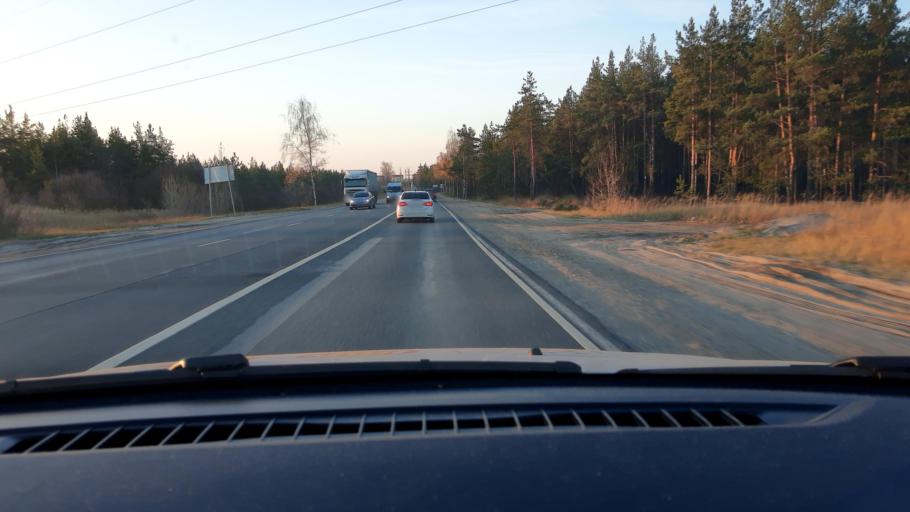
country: RU
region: Nizjnij Novgorod
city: Dzerzhinsk
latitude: 56.2670
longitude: 43.4709
